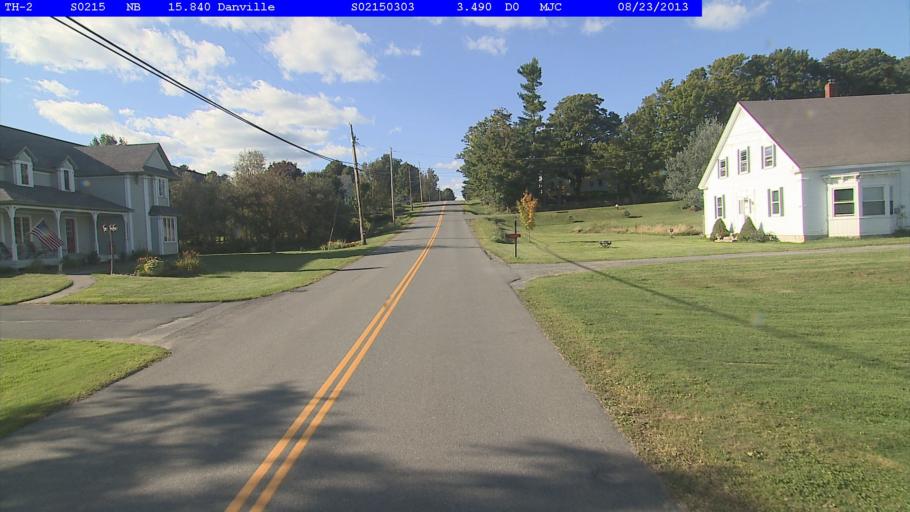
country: US
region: Vermont
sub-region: Caledonia County
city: Saint Johnsbury
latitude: 44.4144
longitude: -72.1410
